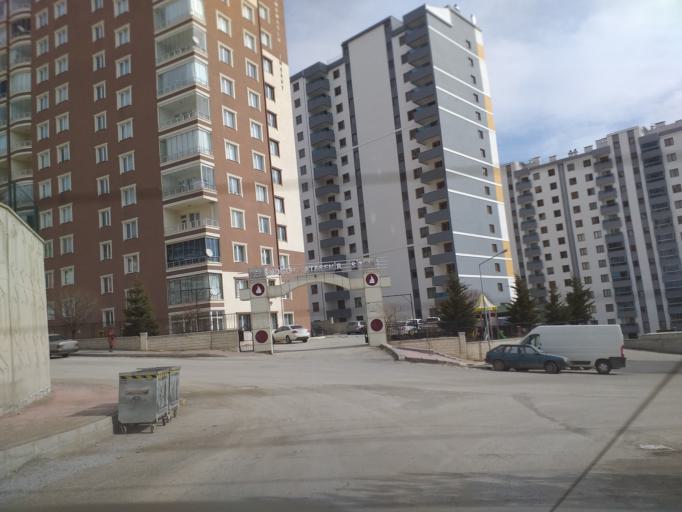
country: TR
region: Yozgat
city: Yozgat
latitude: 39.8322
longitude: 34.8221
